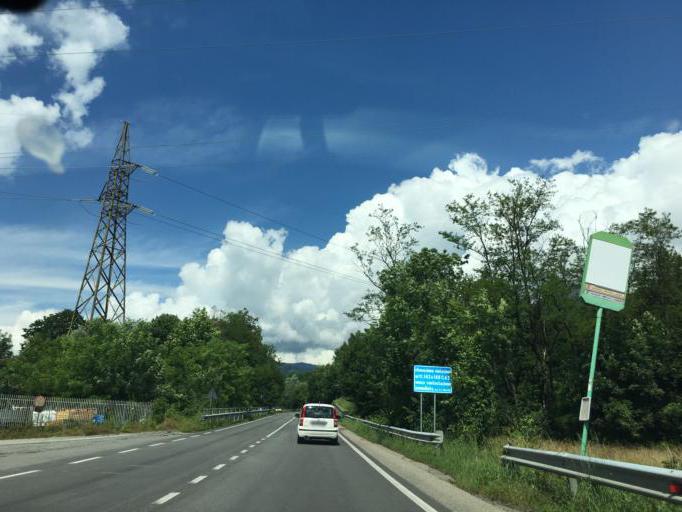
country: IT
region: Lombardy
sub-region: Provincia di Como
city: Codogna-Cardano
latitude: 46.0270
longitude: 9.2048
